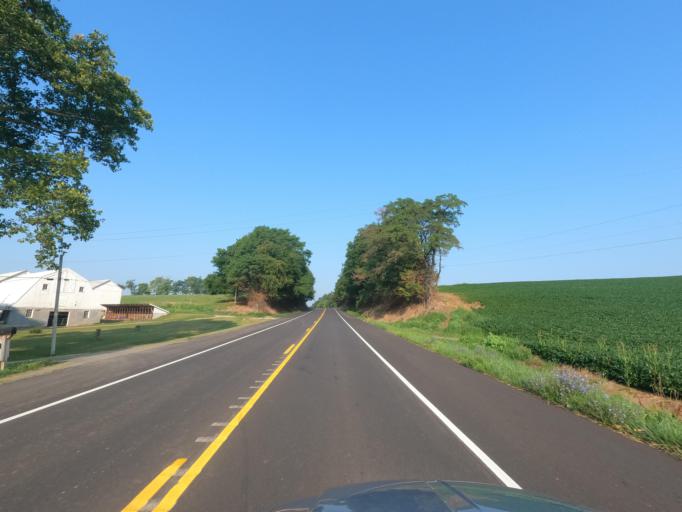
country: US
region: Pennsylvania
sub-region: Franklin County
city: Wayne Heights
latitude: 39.7078
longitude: -77.5827
